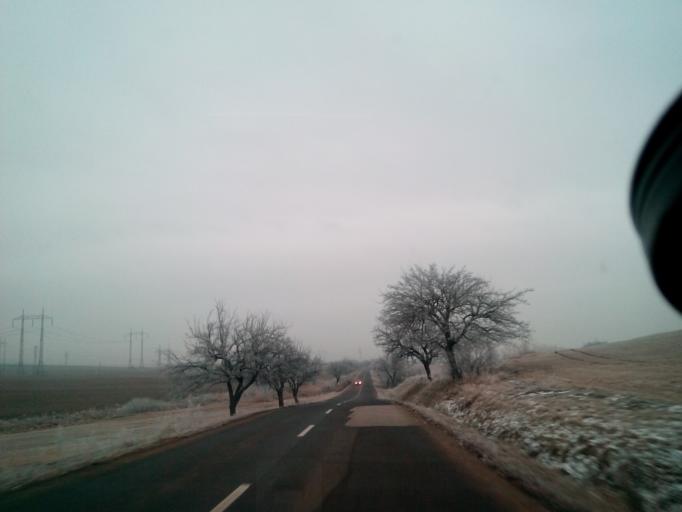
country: SK
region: Presovsky
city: Lubica
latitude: 48.9891
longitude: 20.4258
